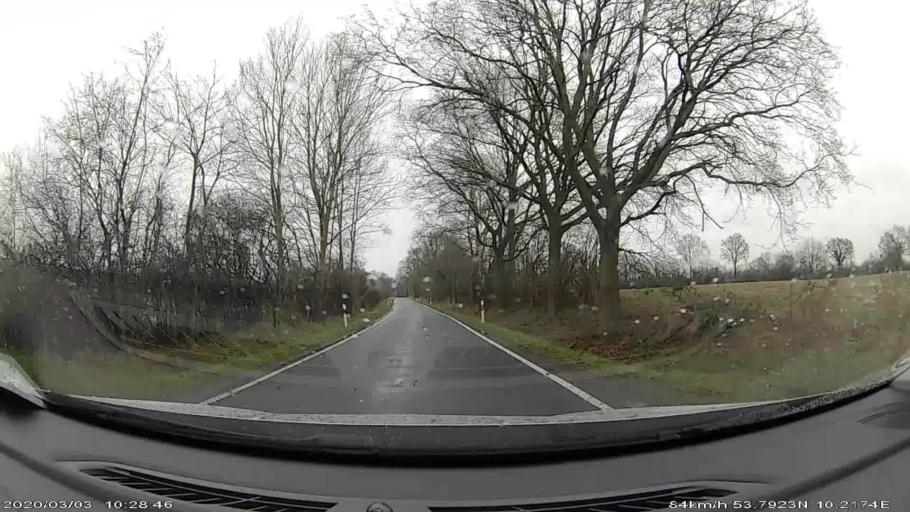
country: DE
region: Schleswig-Holstein
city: Sulfeld
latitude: 53.7939
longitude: 10.2230
